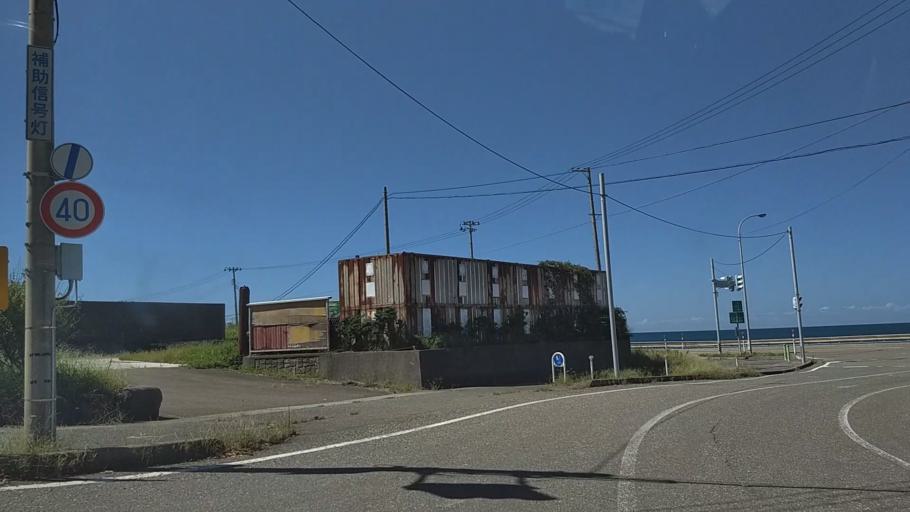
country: JP
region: Niigata
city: Joetsu
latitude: 37.1703
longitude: 138.0937
